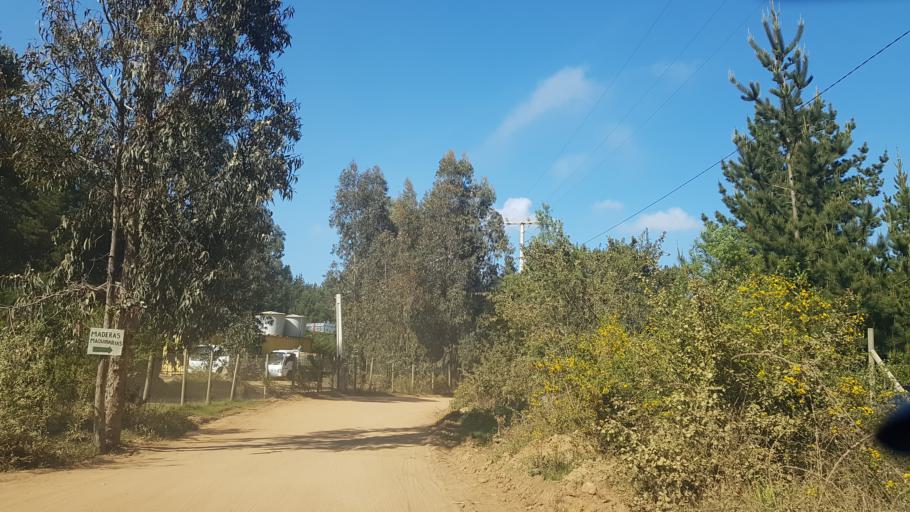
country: CL
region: Valparaiso
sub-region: Provincia de Valparaiso
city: Valparaiso
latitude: -33.1287
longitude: -71.6672
